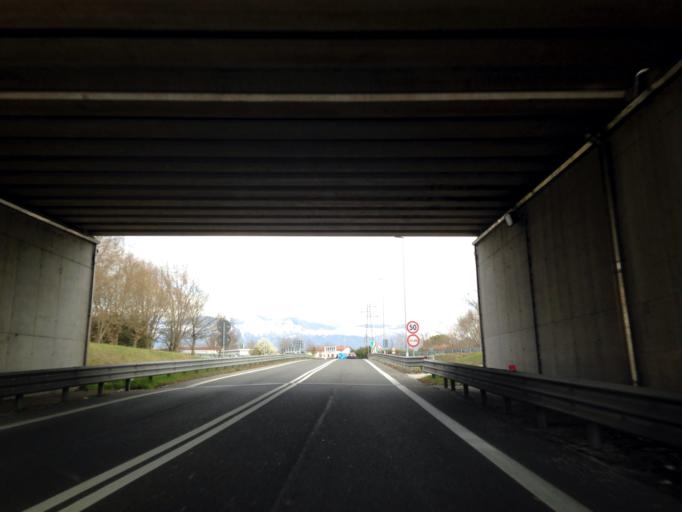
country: IT
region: Friuli Venezia Giulia
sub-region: Provincia di Pordenone
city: Porcia
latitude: 45.9436
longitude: 12.6223
